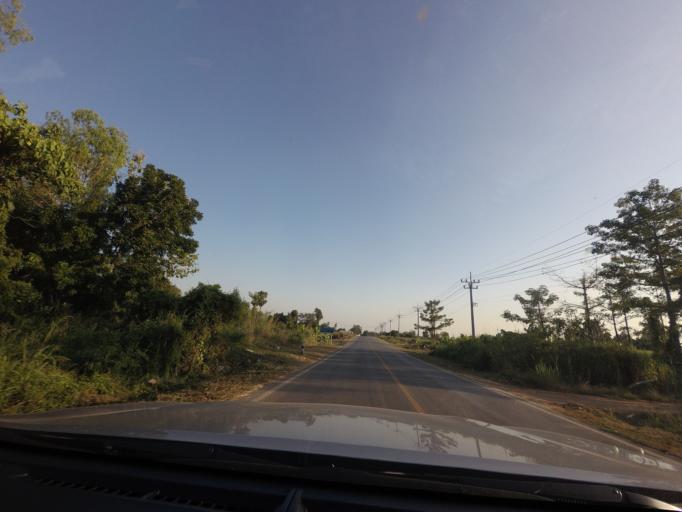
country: TH
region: Sukhothai
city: Sawankhalok
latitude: 17.3559
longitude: 99.8193
